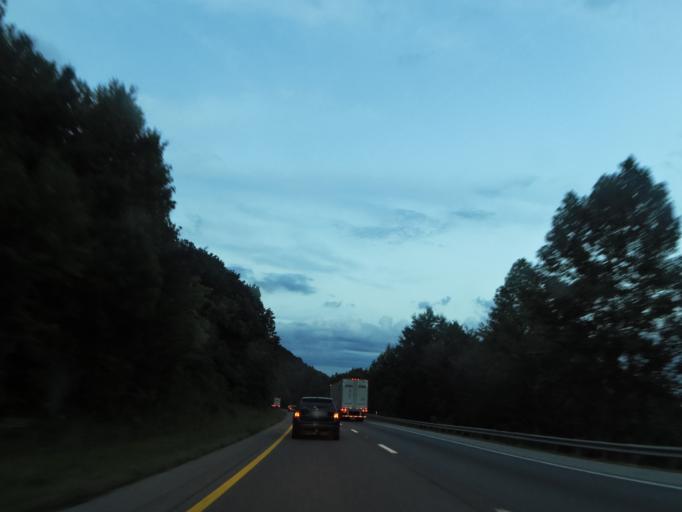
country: US
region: Tennessee
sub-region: Roane County
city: Rockwood
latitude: 35.8928
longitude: -84.6694
